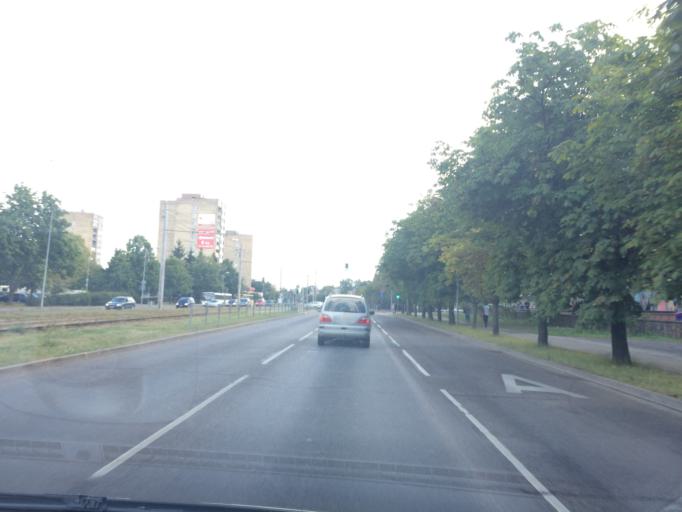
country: LV
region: Kekava
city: Balozi
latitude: 56.9160
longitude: 24.1745
